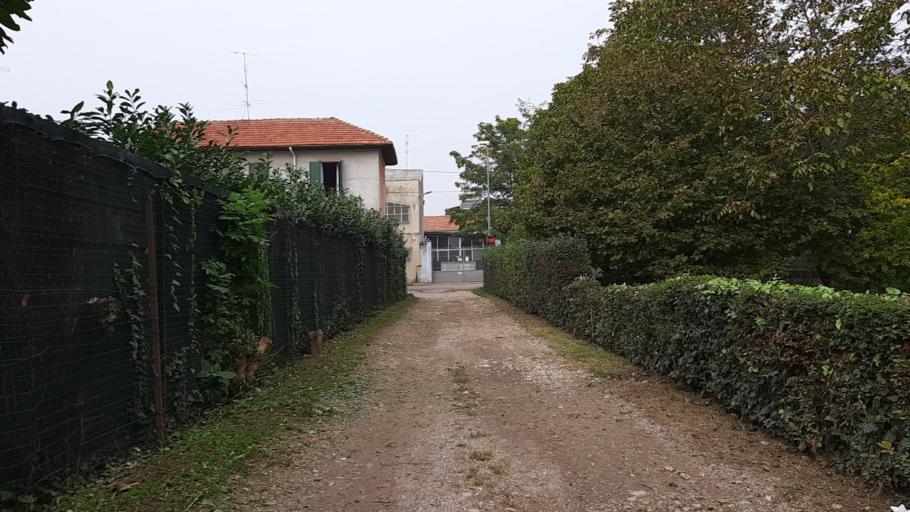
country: IT
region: Lombardy
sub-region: Provincia di Varese
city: Busto Arsizio
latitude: 45.6013
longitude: 8.8533
